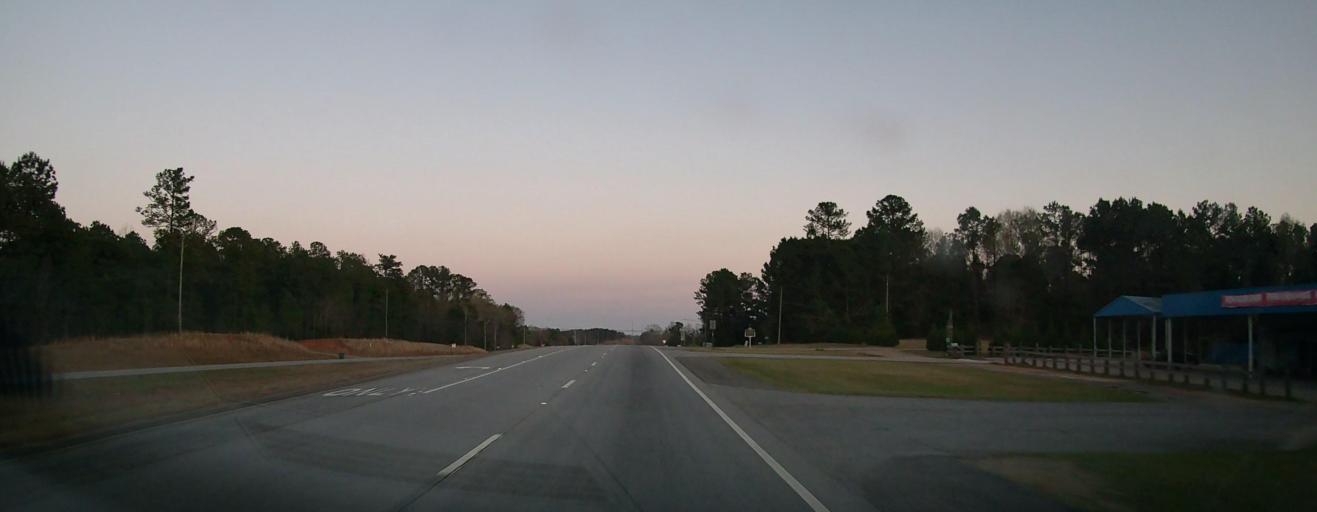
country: US
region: Alabama
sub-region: Tallapoosa County
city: Dadeville
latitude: 32.8640
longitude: -85.7975
